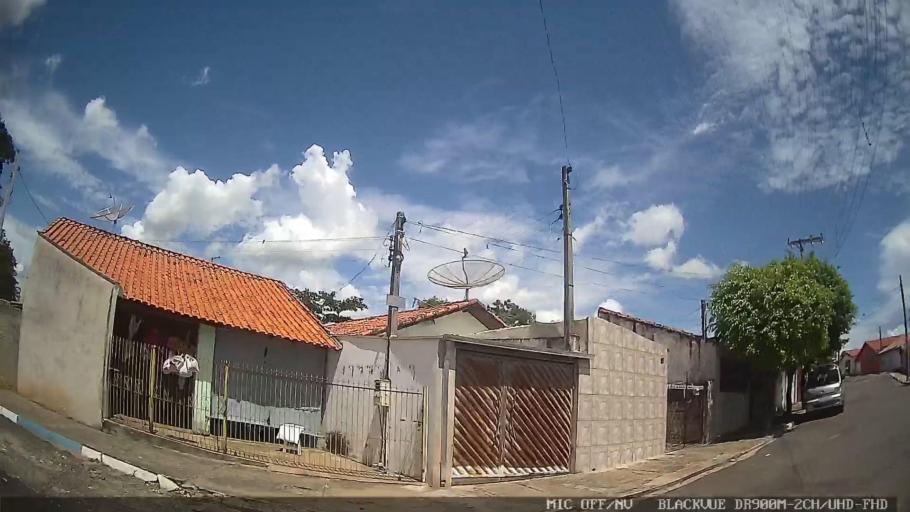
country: BR
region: Sao Paulo
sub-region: Conchas
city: Conchas
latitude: -23.0170
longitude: -48.0177
